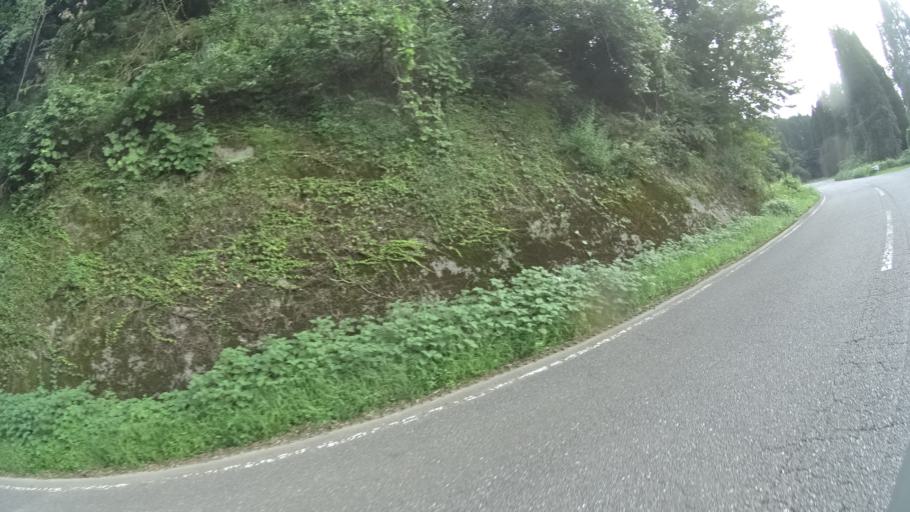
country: JP
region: Kumamoto
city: Ozu
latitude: 32.6902
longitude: 131.0133
